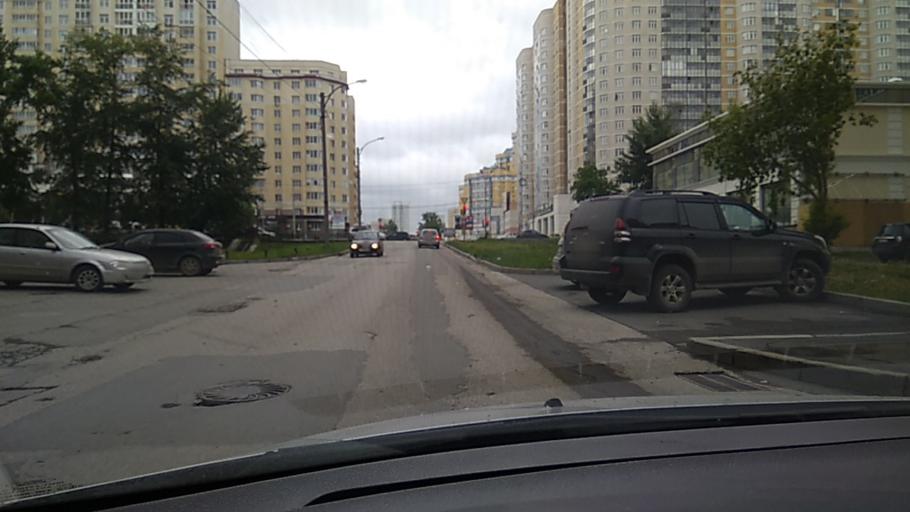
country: RU
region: Sverdlovsk
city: Yekaterinburg
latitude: 56.8029
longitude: 60.6137
